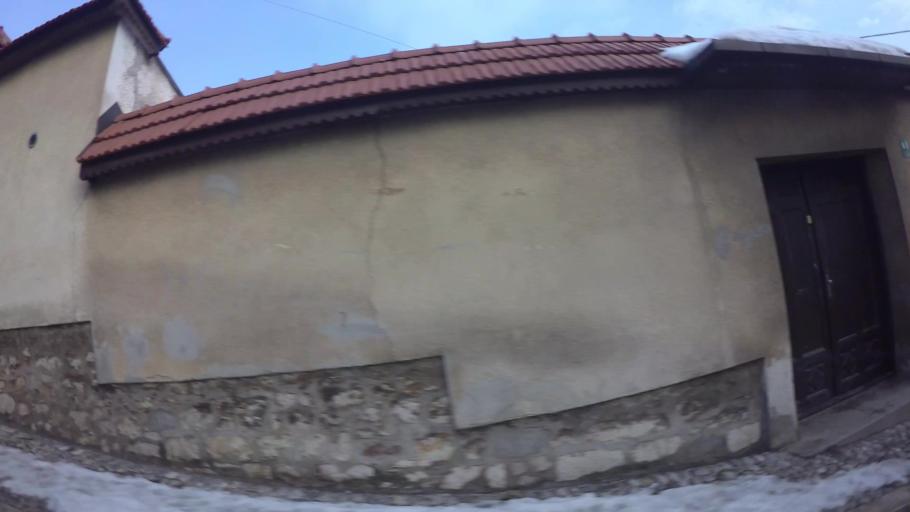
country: BA
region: Federation of Bosnia and Herzegovina
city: Kobilja Glava
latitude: 43.8641
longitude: 18.4299
